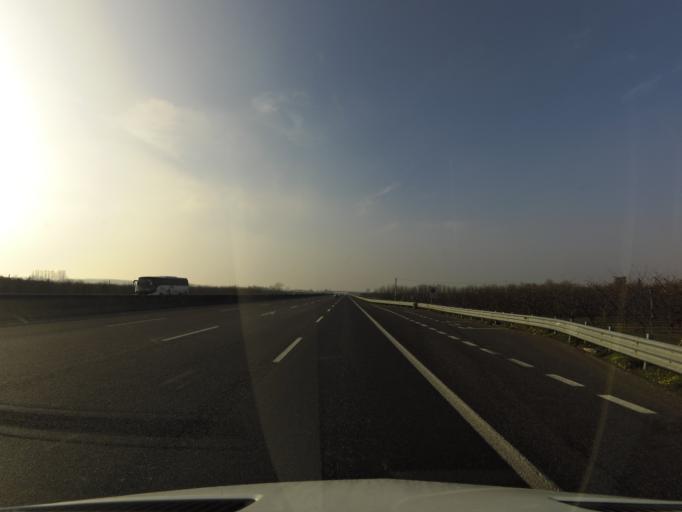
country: IT
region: Emilia-Romagna
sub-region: Provincia di Modena
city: San Cesario sul Panaro
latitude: 44.5689
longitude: 11.0251
